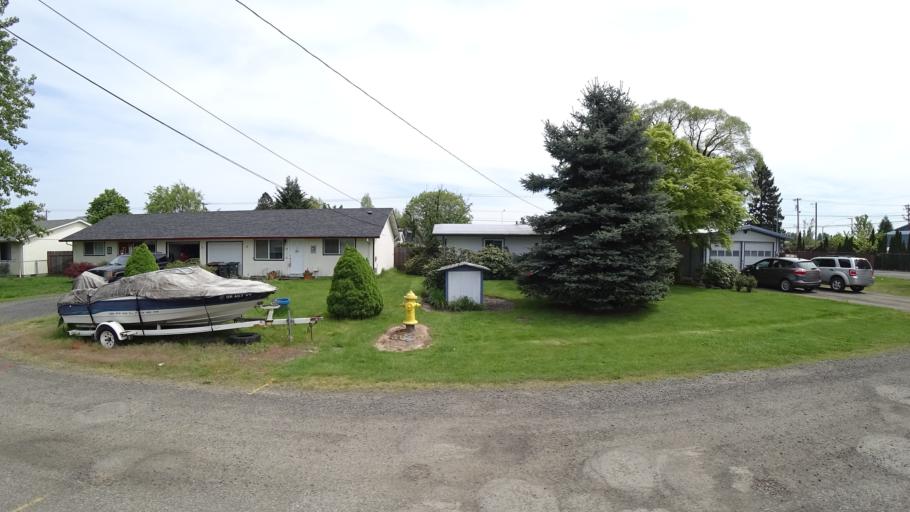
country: US
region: Oregon
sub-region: Washington County
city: Hillsboro
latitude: 45.5019
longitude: -122.9321
